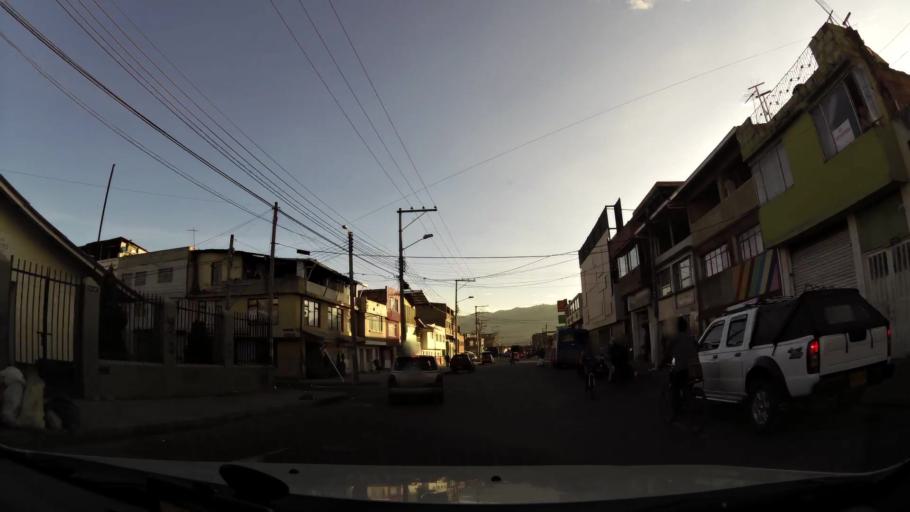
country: CO
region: Bogota D.C.
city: Bogota
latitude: 4.5634
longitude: -74.1294
